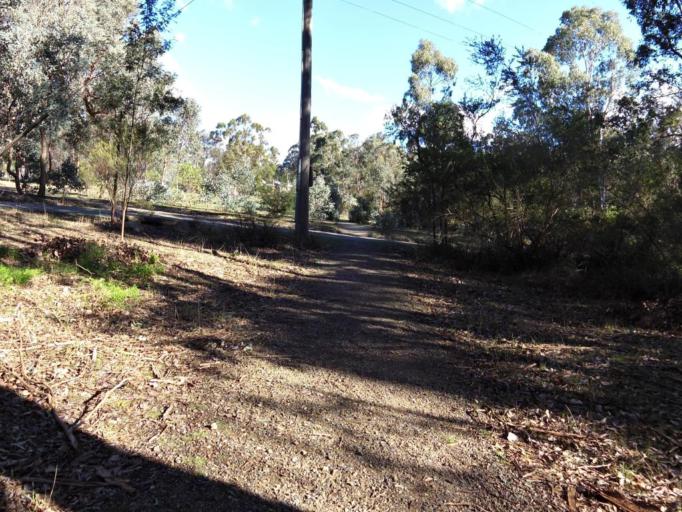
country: AU
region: Victoria
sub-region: Nillumbik
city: North Warrandyte
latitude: -37.7335
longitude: 145.2095
